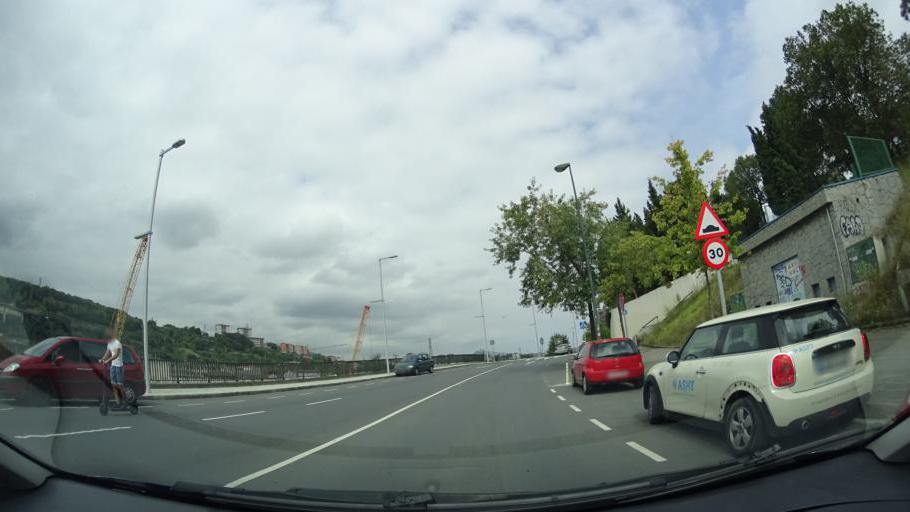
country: ES
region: Basque Country
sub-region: Bizkaia
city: Bilbao
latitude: 43.2709
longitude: -2.9592
